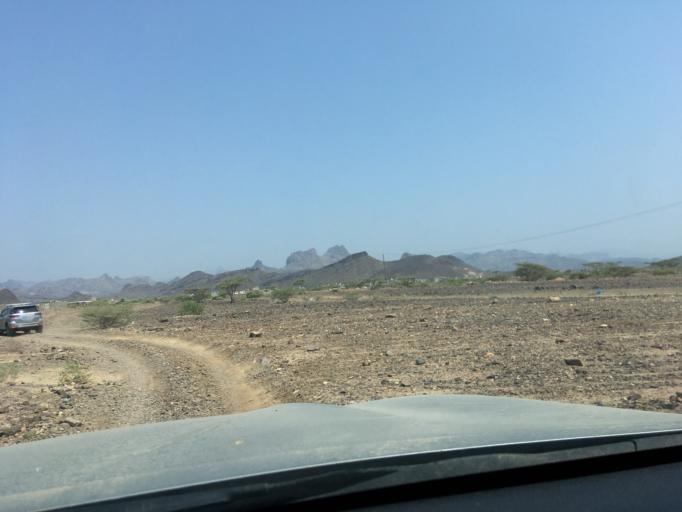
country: YE
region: Lahij
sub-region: Al Milah
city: Al Milah
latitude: 13.4332
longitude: 44.8205
